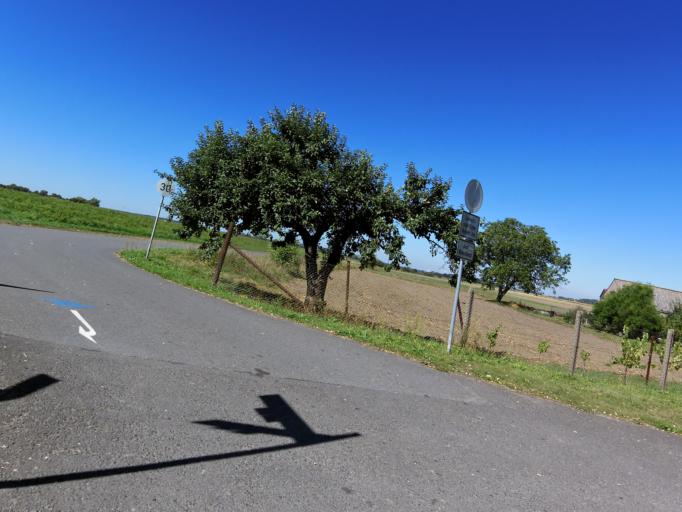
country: DE
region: Saxony-Anhalt
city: Pretzsch
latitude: 51.7204
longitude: 12.8205
